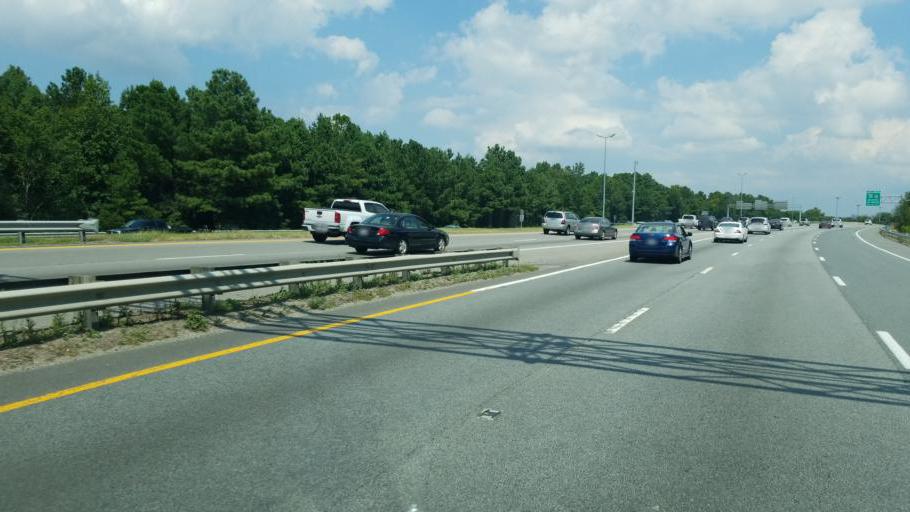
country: US
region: Virginia
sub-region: City of Portsmouth
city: Portsmouth Heights
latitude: 36.7856
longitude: -76.4182
